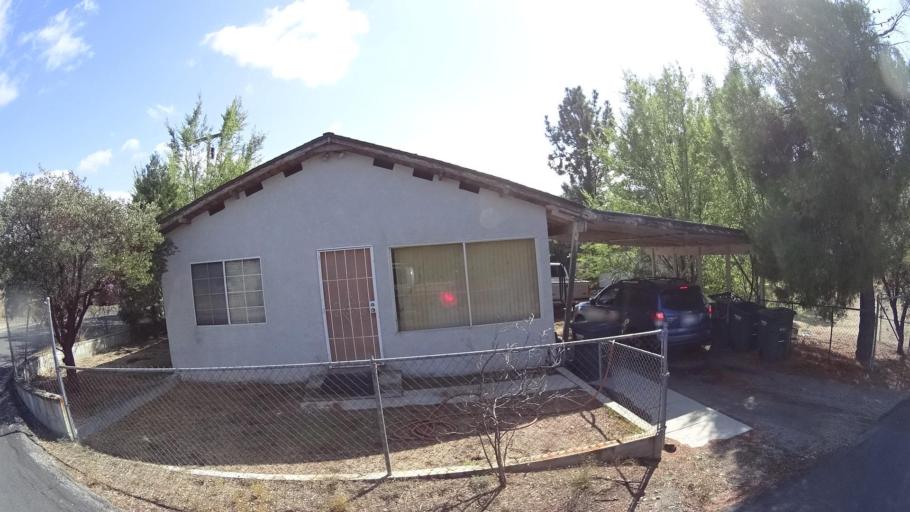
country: US
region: California
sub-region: San Diego County
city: Campo
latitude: 32.6822
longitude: -116.5083
